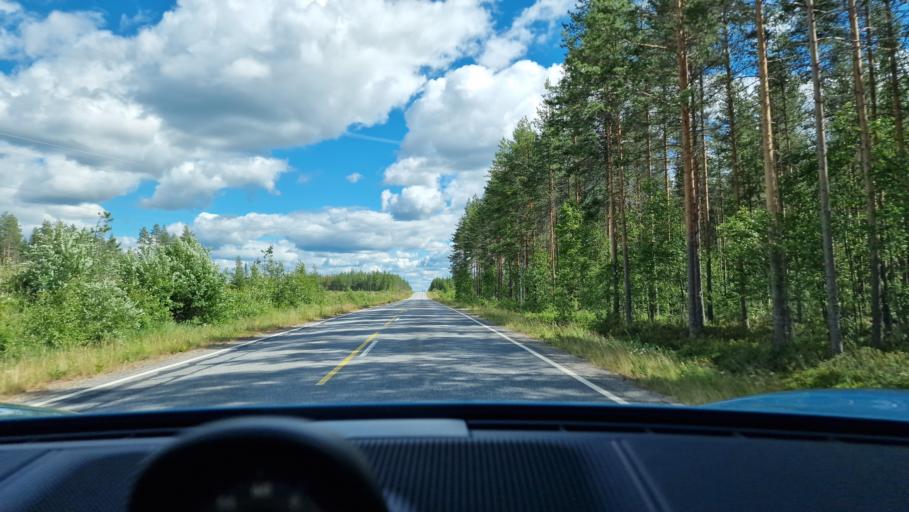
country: FI
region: Central Finland
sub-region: Saarijaervi-Viitasaari
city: Pylkoenmaeki
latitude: 62.6635
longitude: 24.5512
